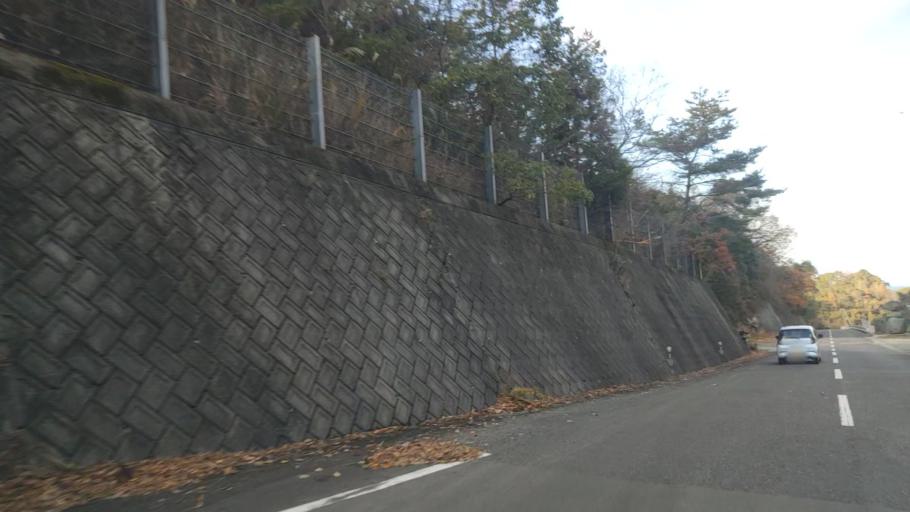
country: JP
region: Ehime
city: Saijo
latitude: 33.8849
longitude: 133.1292
